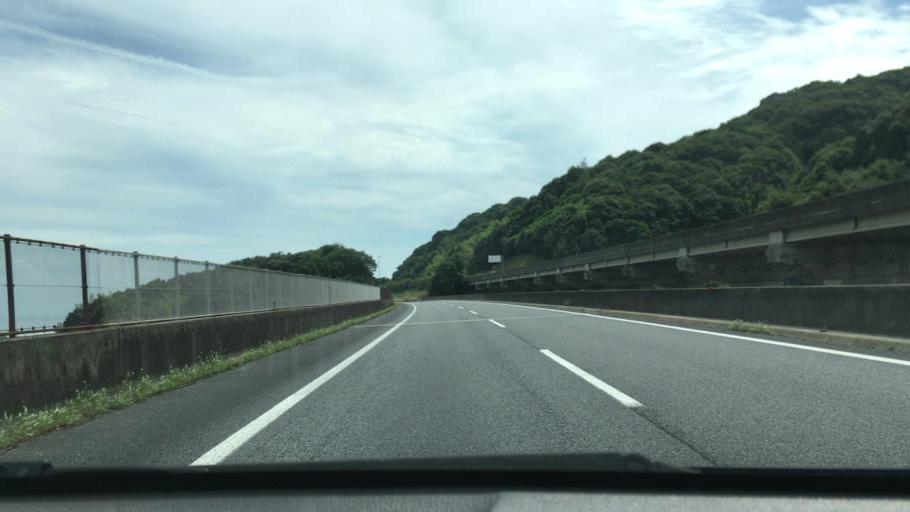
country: JP
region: Yamaguchi
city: Hofu
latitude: 34.0680
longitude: 131.6594
